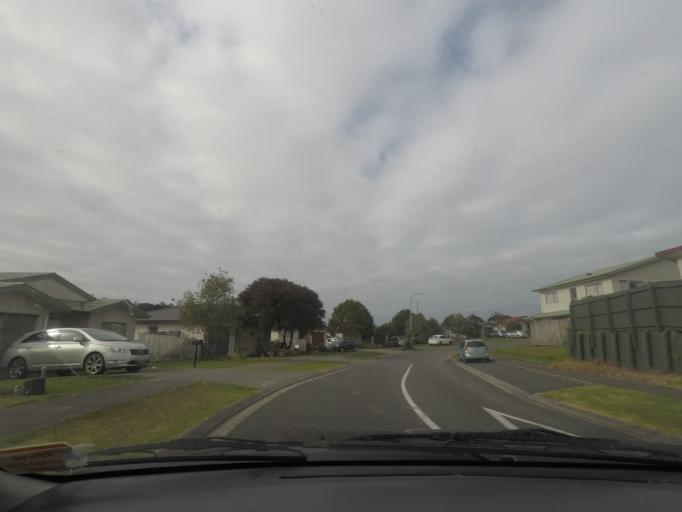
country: NZ
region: Auckland
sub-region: Auckland
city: Waitakere
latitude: -36.9060
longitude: 174.6333
